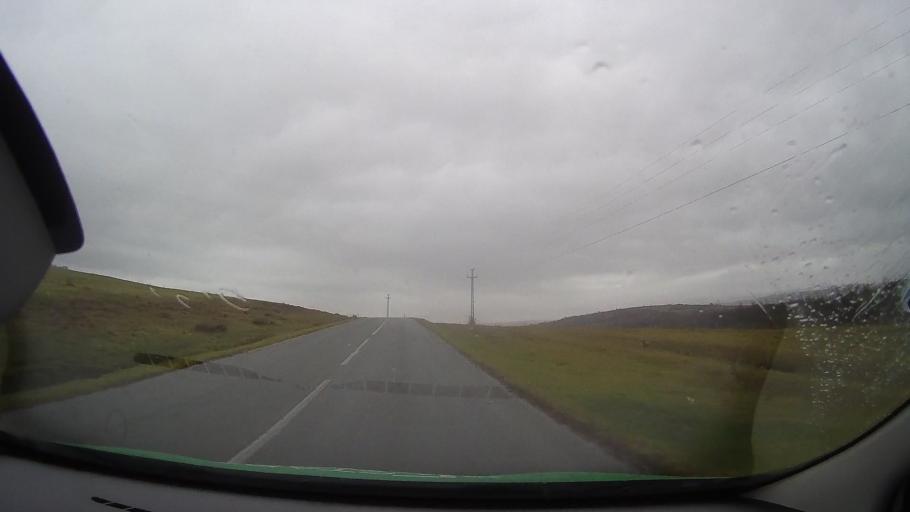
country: RO
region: Mures
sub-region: Comuna Brancovenesti
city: Valenii de Mures
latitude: 46.9144
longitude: 24.7808
